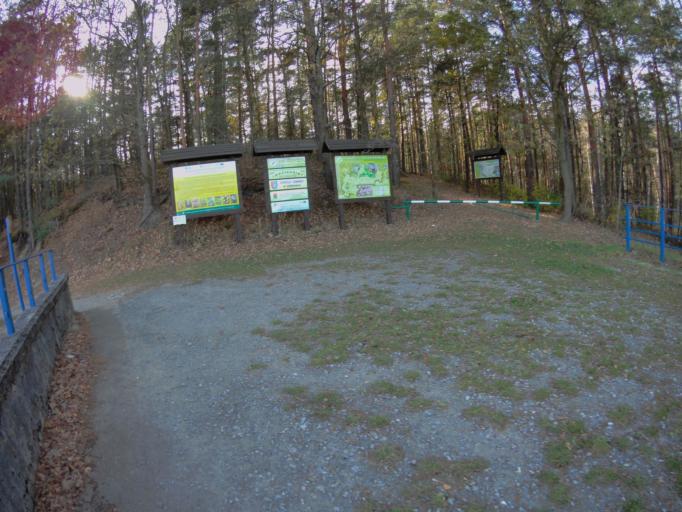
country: PL
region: Subcarpathian Voivodeship
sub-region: Powiat kolbuszowski
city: Lipnica
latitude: 50.3398
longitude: 21.9291
